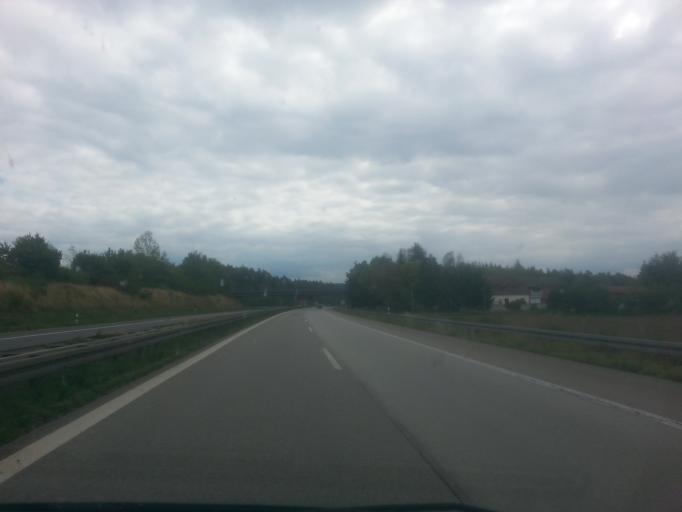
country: DE
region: Bavaria
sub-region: Upper Palatinate
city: Teublitz
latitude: 49.2460
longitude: 12.1308
